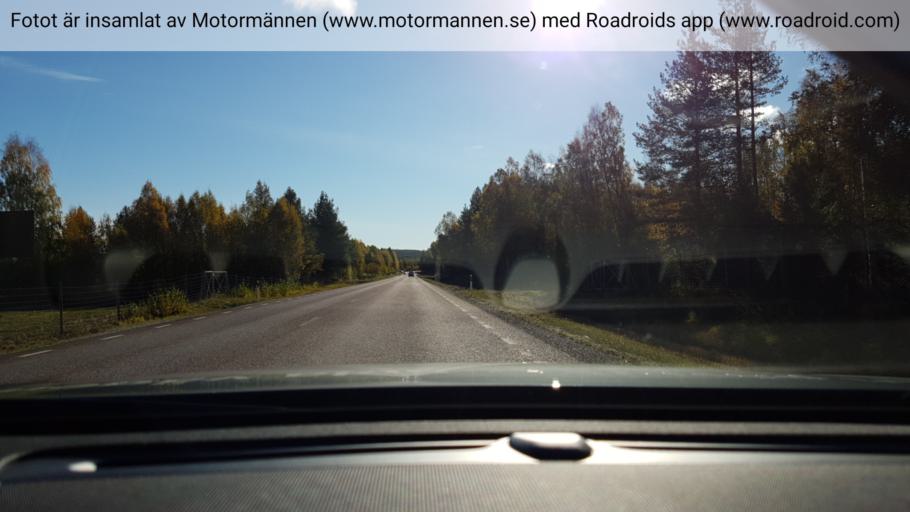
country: SE
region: Vaesterbotten
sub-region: Skelleftea Kommun
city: Burea
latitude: 64.6102
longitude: 21.1879
